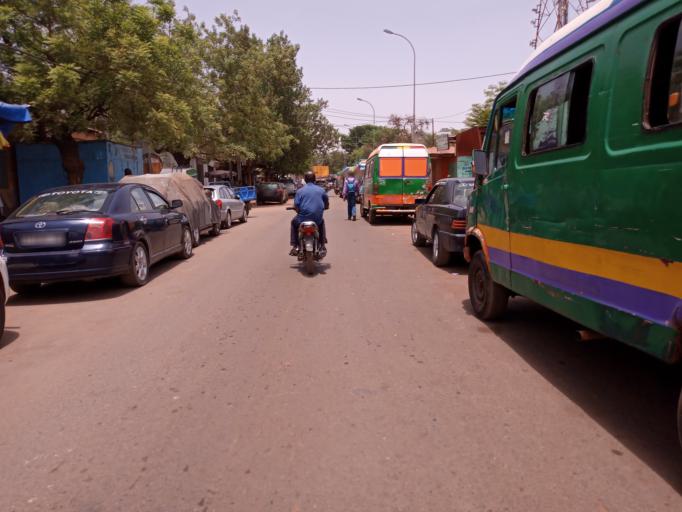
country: ML
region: Bamako
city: Bamako
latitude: 12.6423
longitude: -8.0014
